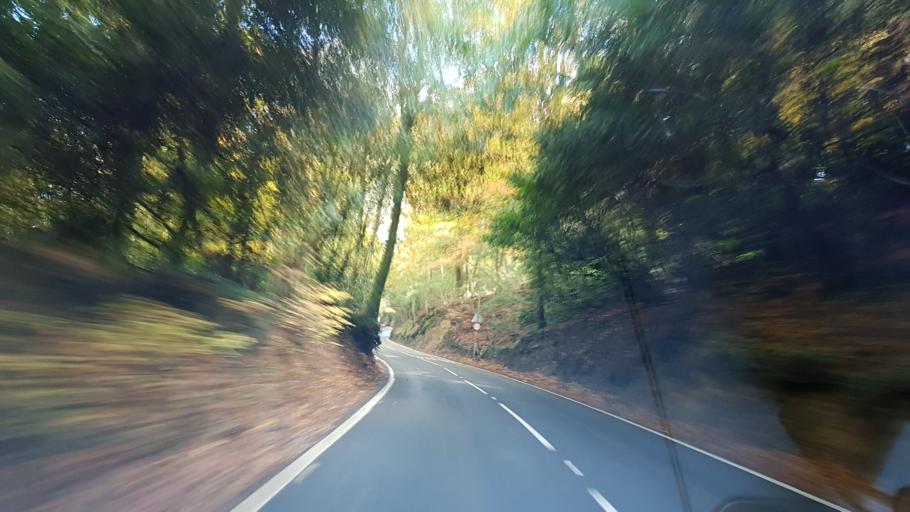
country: GB
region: England
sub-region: Surrey
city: Hindhead
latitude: 51.0979
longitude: -0.7401
